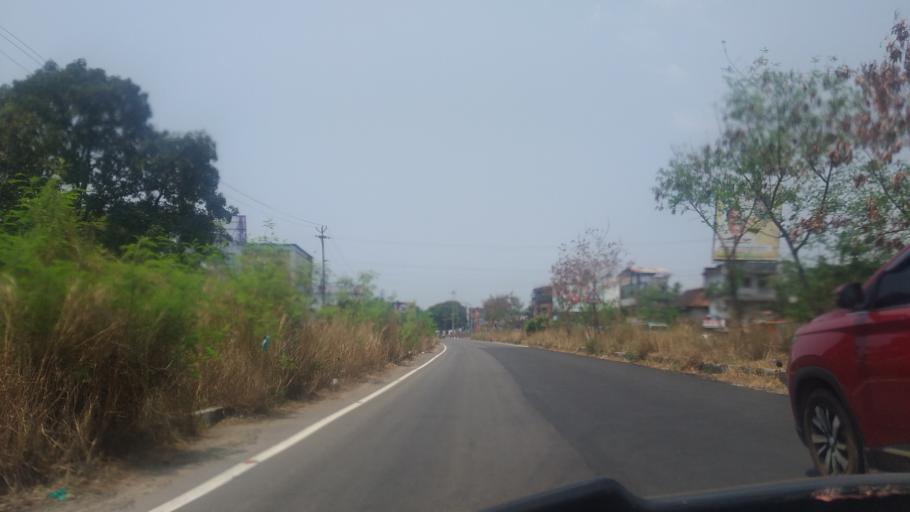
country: IN
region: Kerala
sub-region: Thrissur District
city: Kodungallur
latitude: 10.2313
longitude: 76.1952
